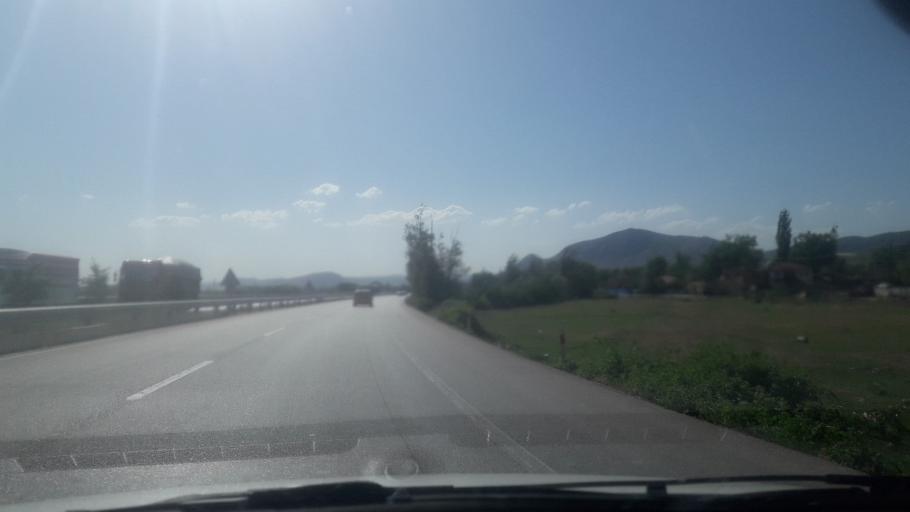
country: TR
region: Tokat
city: Dokmetepe
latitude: 40.3135
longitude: 36.2616
